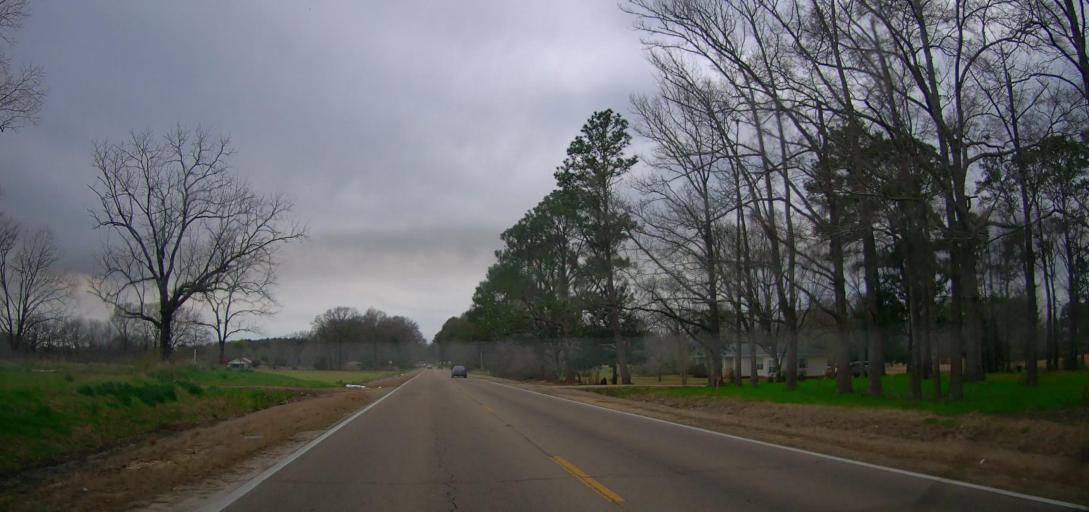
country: US
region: Mississippi
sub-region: Lee County
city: Plantersville
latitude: 34.2657
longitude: -88.6296
